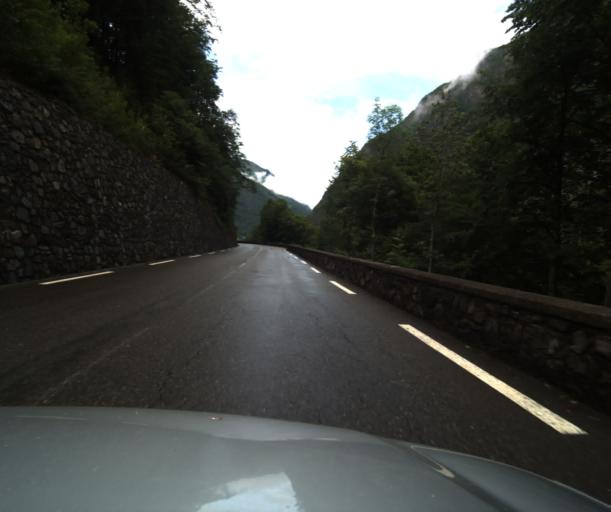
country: FR
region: Midi-Pyrenees
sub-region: Departement des Hautes-Pyrenees
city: Luz-Saint-Sauveur
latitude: 42.8289
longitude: 0.0065
